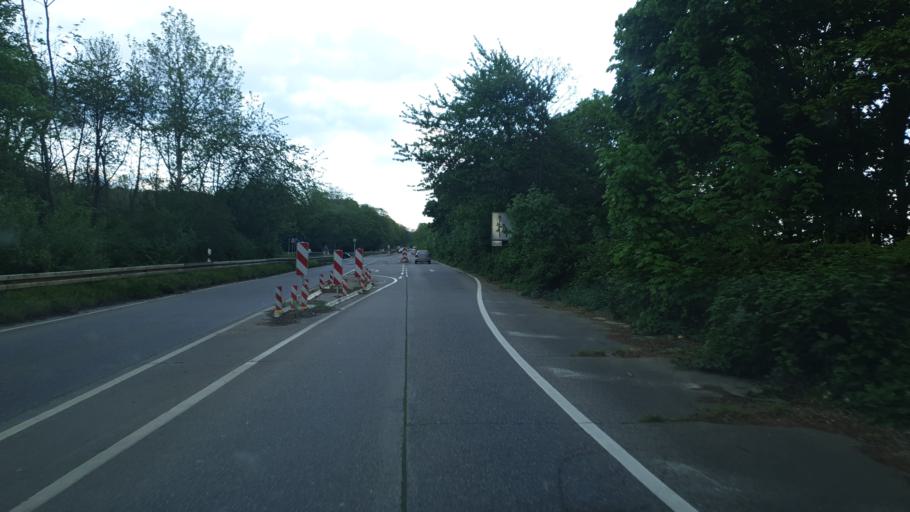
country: DE
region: North Rhine-Westphalia
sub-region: Regierungsbezirk Koln
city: Kerpen
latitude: 50.9238
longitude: 6.7022
